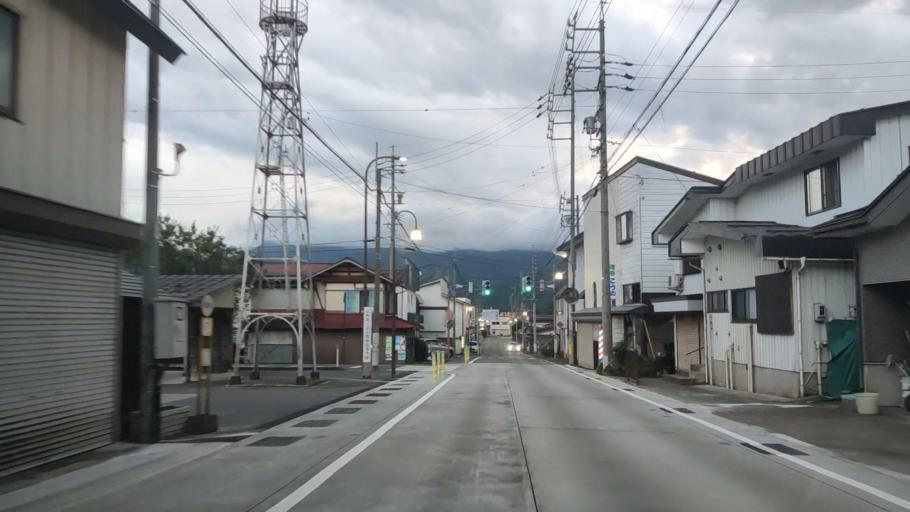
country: JP
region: Nagano
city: Iiyama
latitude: 36.8635
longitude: 138.4061
